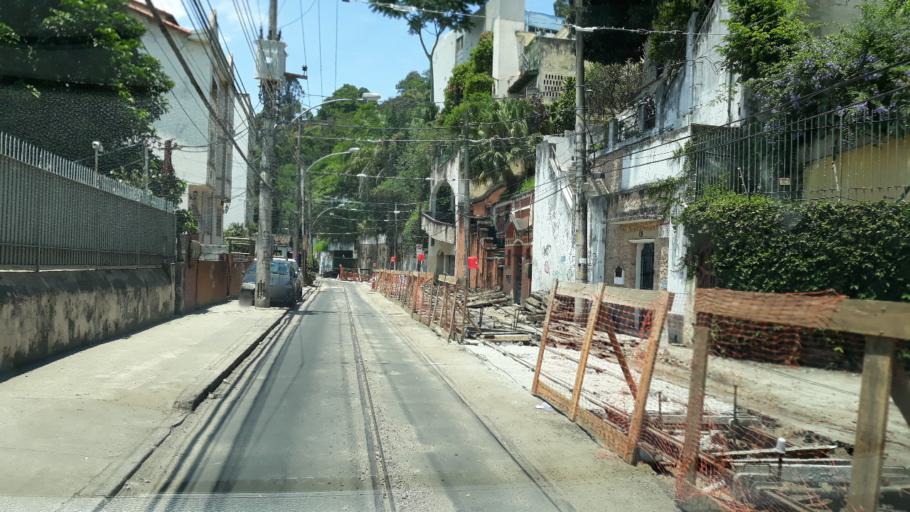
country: BR
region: Rio de Janeiro
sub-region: Rio De Janeiro
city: Rio de Janeiro
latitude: -22.9320
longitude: -43.1971
